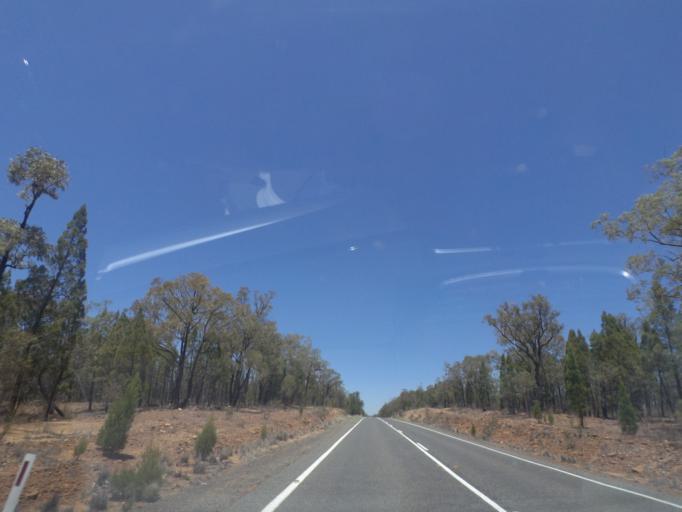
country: AU
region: New South Wales
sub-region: Narrabri
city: Narrabri
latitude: -30.7023
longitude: 149.5340
